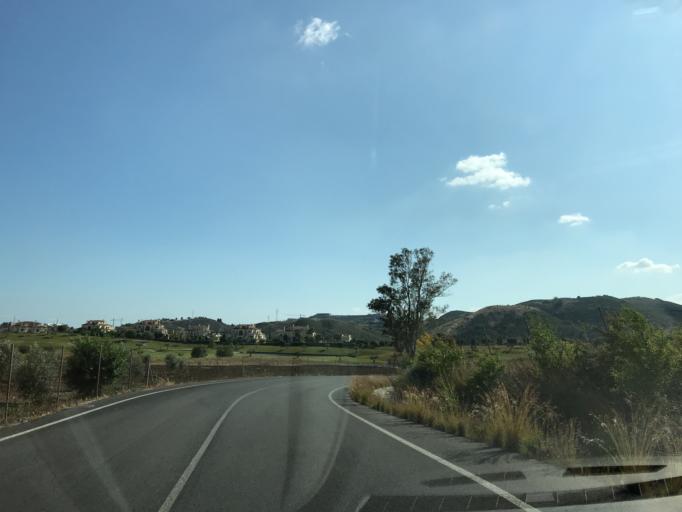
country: ES
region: Andalusia
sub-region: Provincia de Malaga
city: Benahavis
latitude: 36.5065
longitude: -5.0197
